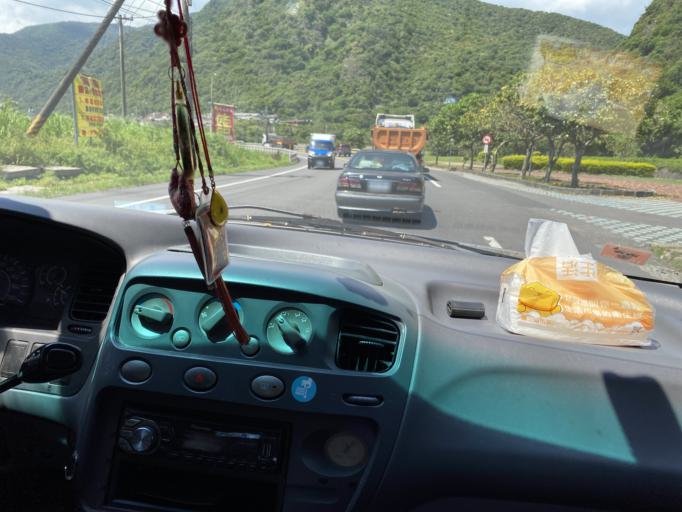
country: TW
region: Taiwan
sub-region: Yilan
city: Yilan
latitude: 24.9421
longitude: 121.8967
